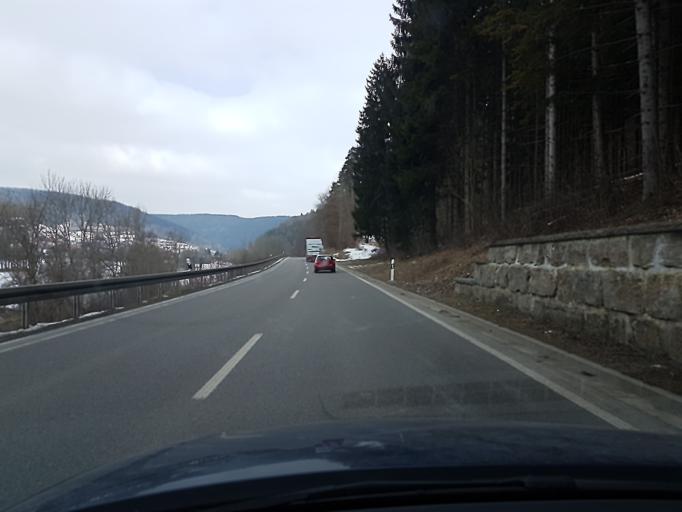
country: DE
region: Baden-Wuerttemberg
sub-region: Freiburg Region
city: Sulz am Neckar
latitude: 48.4055
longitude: 8.6420
